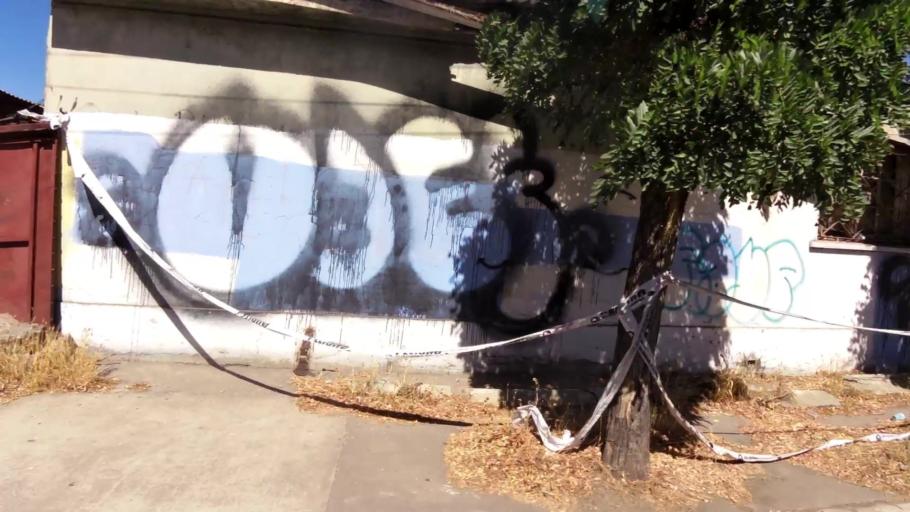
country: CL
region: O'Higgins
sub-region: Provincia de Colchagua
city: Chimbarongo
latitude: -34.5833
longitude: -70.9927
